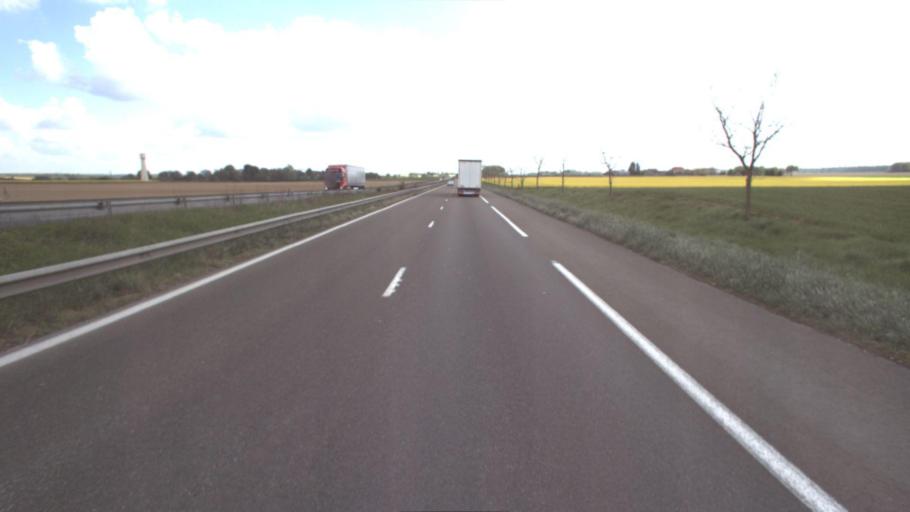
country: FR
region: Ile-de-France
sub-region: Departement de Seine-et-Marne
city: Rozay-en-Brie
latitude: 48.6864
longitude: 2.9838
